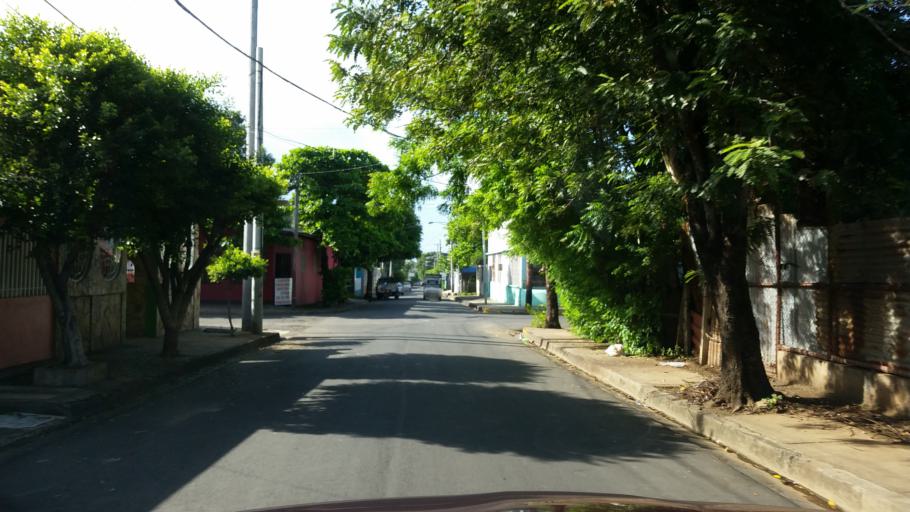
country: NI
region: Managua
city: Managua
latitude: 12.1468
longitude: -86.2691
